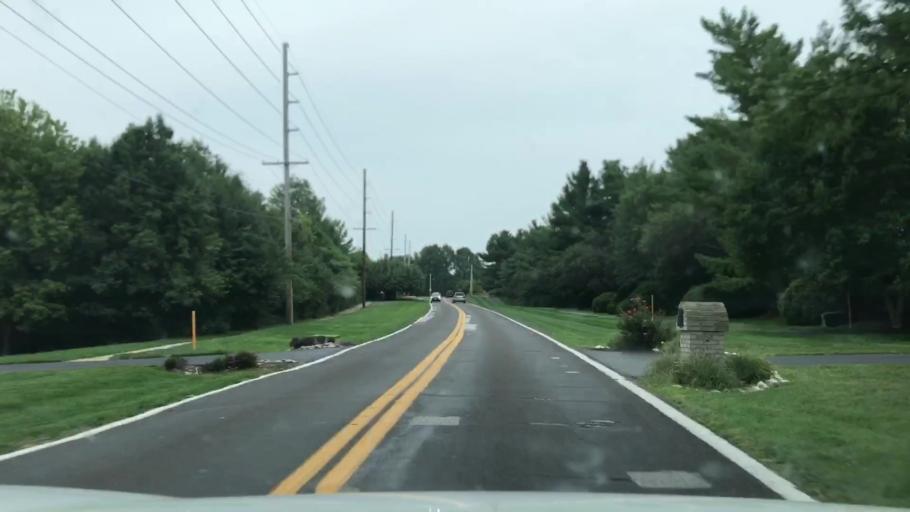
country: US
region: Missouri
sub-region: Saint Louis County
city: Clarkson Valley
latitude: 38.6304
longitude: -90.5990
